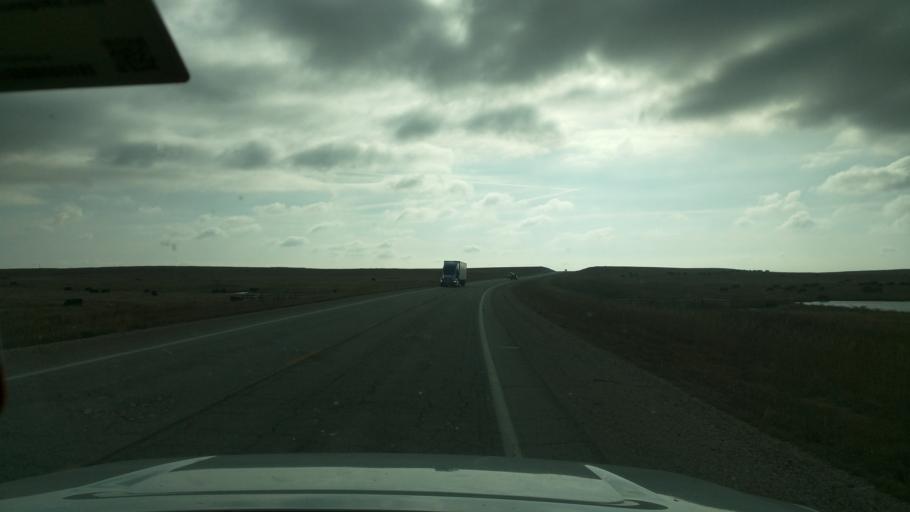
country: US
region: Kansas
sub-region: Chautauqua County
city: Sedan
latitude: 37.1004
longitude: -96.2354
